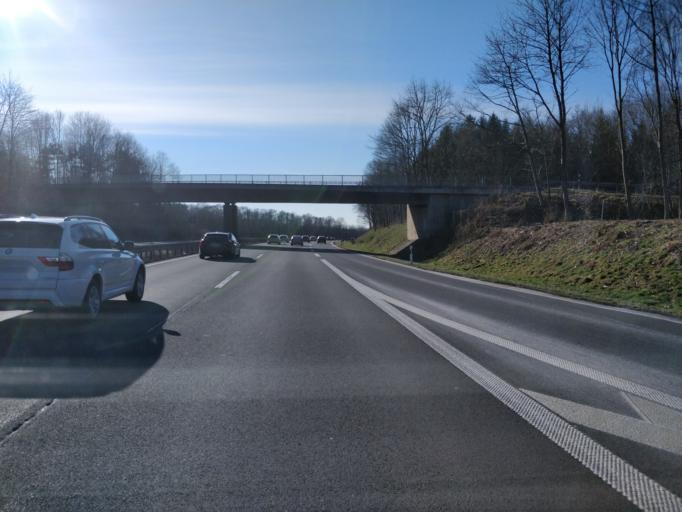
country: DE
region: North Rhine-Westphalia
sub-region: Regierungsbezirk Koln
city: Engelskirchen
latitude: 50.9669
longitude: 7.3629
